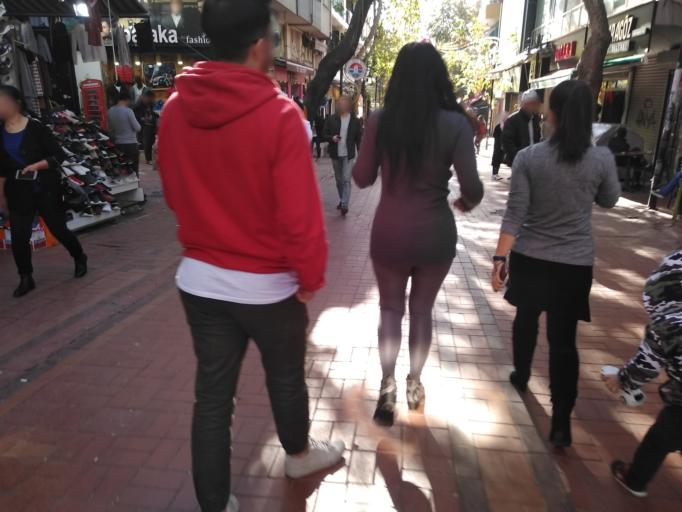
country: TR
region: Istanbul
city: Maltepe
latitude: 40.9230
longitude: 29.1299
